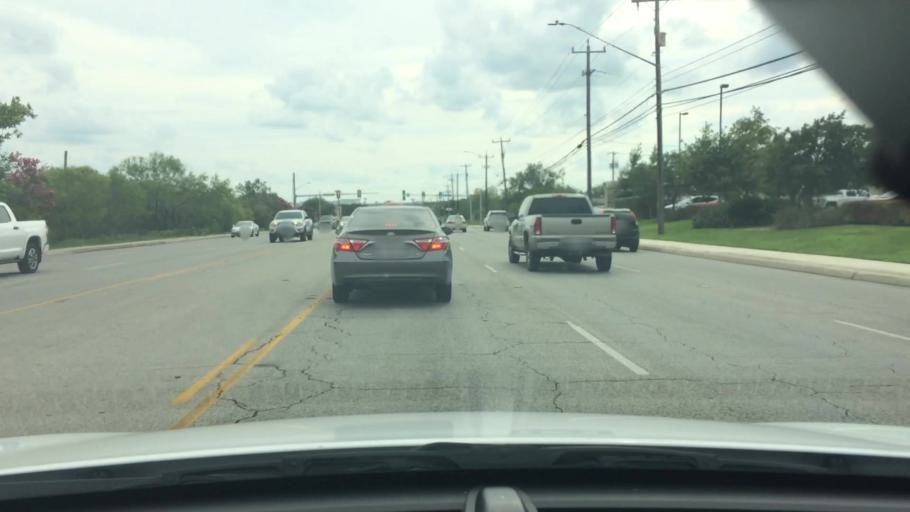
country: US
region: Texas
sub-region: Bexar County
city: Leon Valley
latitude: 29.5371
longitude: -98.5865
